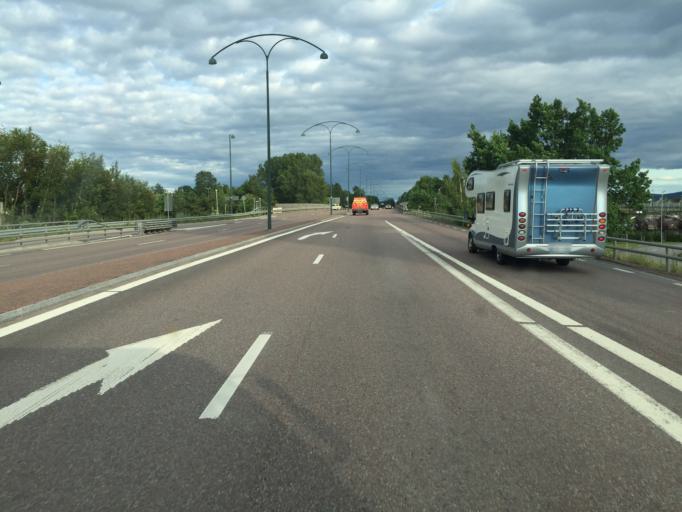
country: SE
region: Dalarna
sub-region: Borlange Kommun
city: Borlaenge
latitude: 60.4829
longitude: 15.4228
